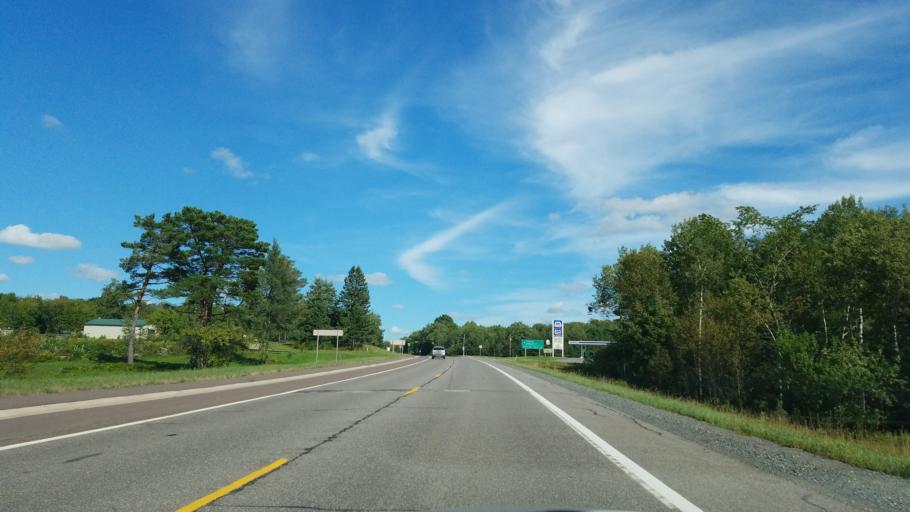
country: US
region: Michigan
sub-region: Baraga County
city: L'Anse
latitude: 46.5458
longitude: -88.5408
